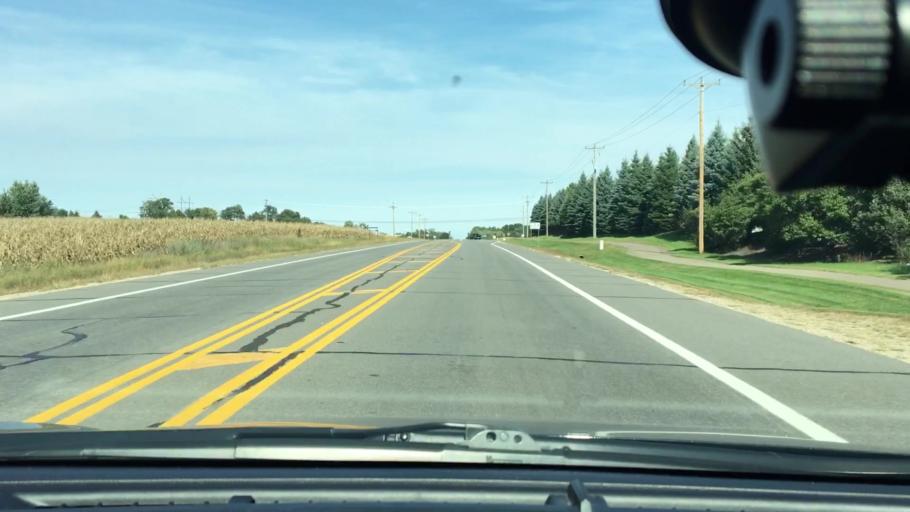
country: US
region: Minnesota
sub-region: Wright County
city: Hanover
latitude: 45.1718
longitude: -93.6657
